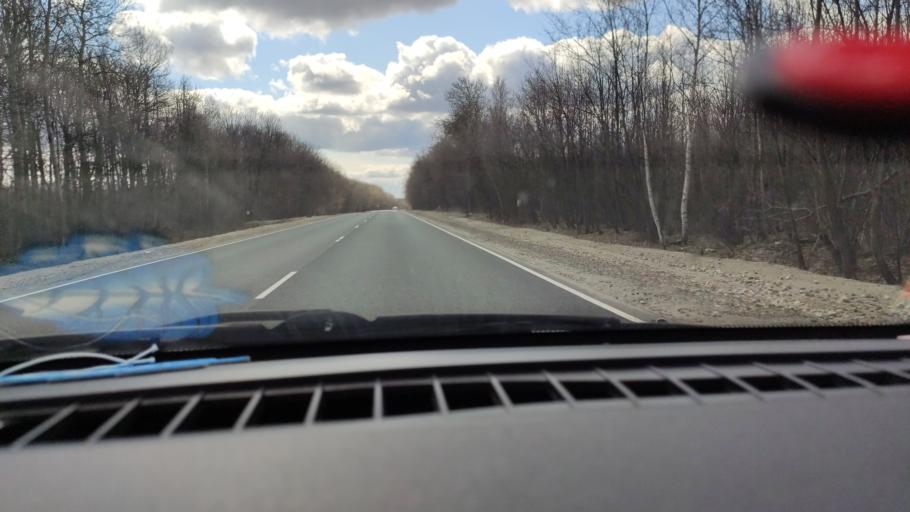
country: RU
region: Saratov
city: Khvalynsk
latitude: 52.4633
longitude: 48.0177
